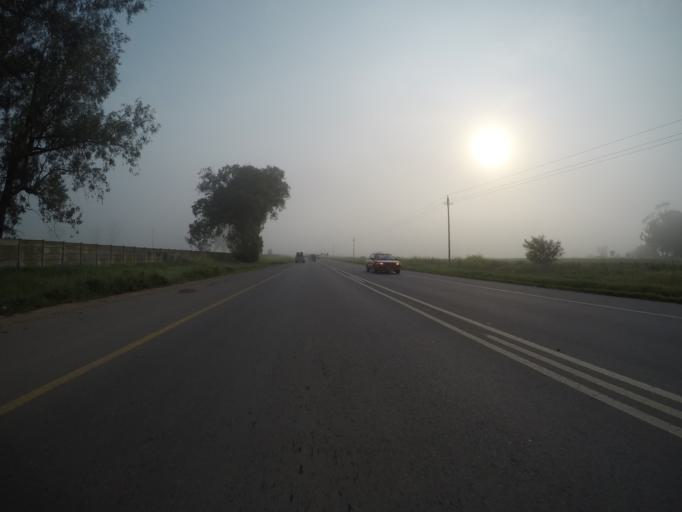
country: ZA
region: Western Cape
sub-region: City of Cape Town
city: Kraaifontein
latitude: -33.7873
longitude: 18.7010
